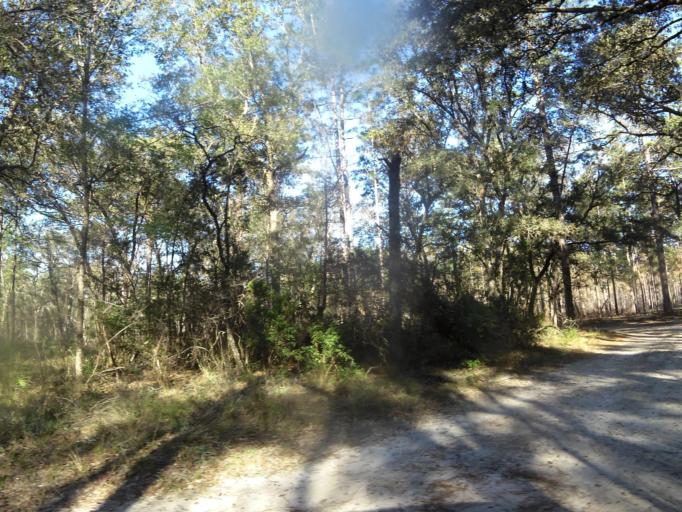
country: US
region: Florida
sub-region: Clay County
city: Middleburg
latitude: 30.1411
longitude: -81.9061
